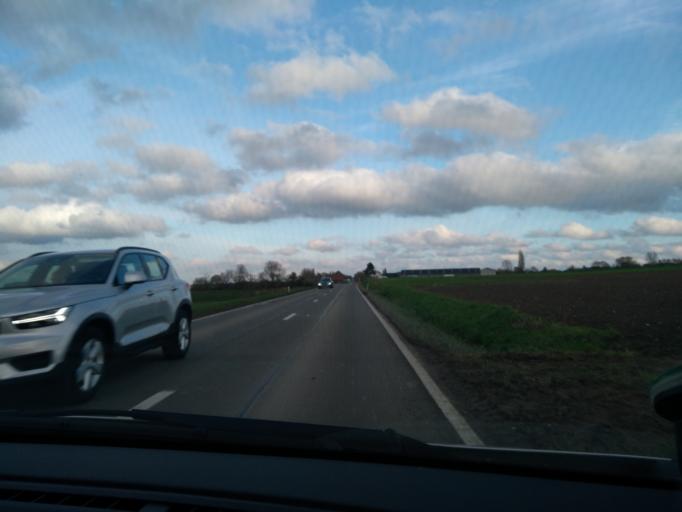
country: BE
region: Wallonia
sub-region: Province du Hainaut
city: Estinnes-au-Val
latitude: 50.3813
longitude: 4.0543
